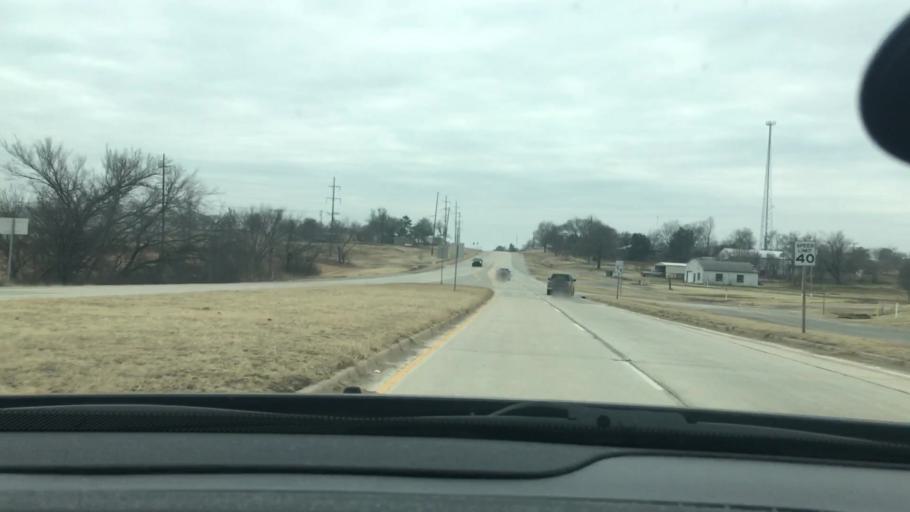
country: US
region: Oklahoma
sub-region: Carter County
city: Healdton
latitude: 34.4480
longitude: -97.5097
